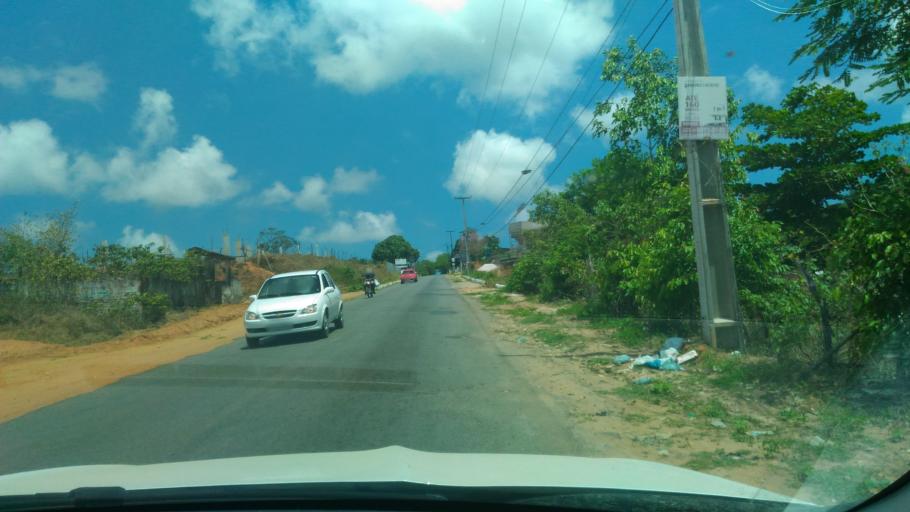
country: BR
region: Paraiba
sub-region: Conde
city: Conde
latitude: -7.2610
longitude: -34.9132
